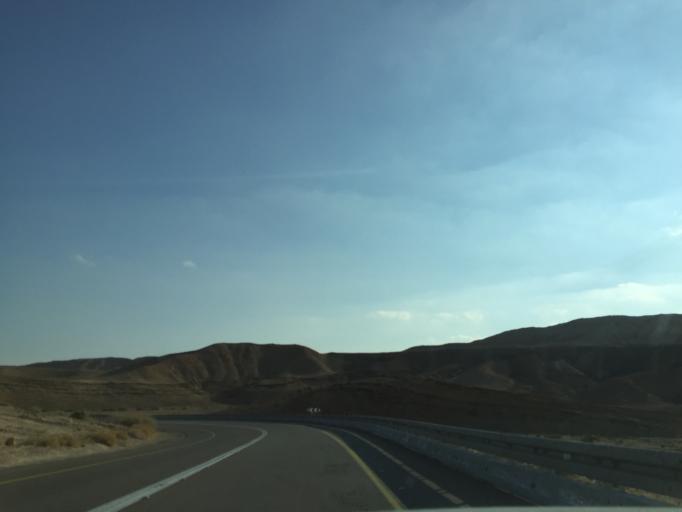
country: IL
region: Southern District
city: `En Boqeq
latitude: 31.1760
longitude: 35.2973
